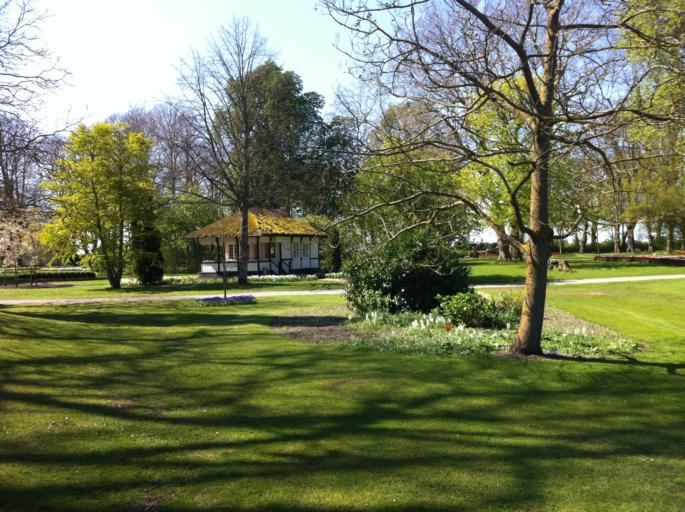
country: DK
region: Zealand
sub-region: Naestved Kommune
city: Naestved
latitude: 55.1888
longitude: 11.7238
